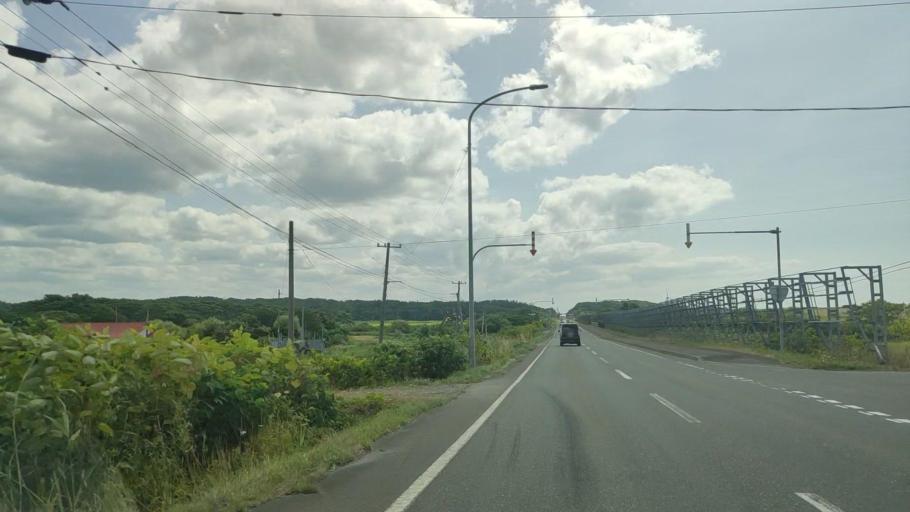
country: JP
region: Hokkaido
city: Makubetsu
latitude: 44.7753
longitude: 141.7918
